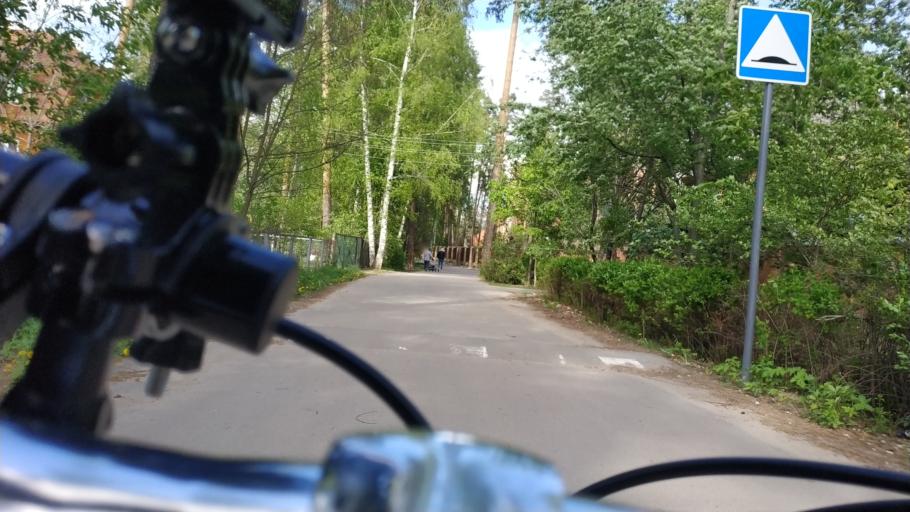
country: RU
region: Moskovskaya
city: Kratovo
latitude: 55.5747
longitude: 38.1954
